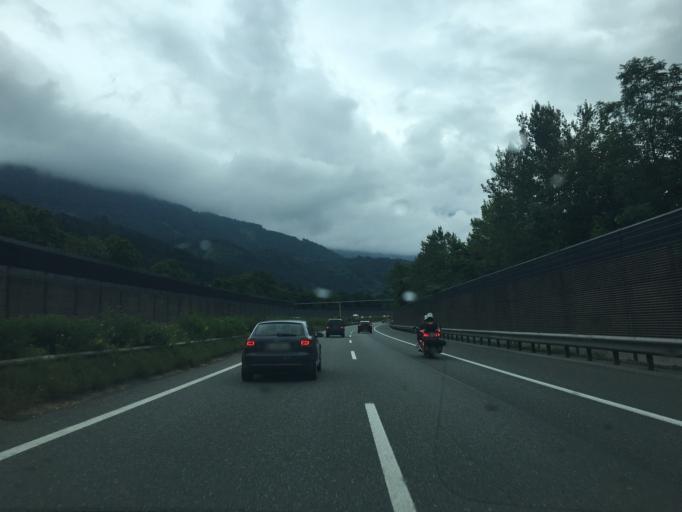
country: AT
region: Tyrol
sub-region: Politischer Bezirk Schwaz
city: Vomp
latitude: 47.3420
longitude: 11.6866
